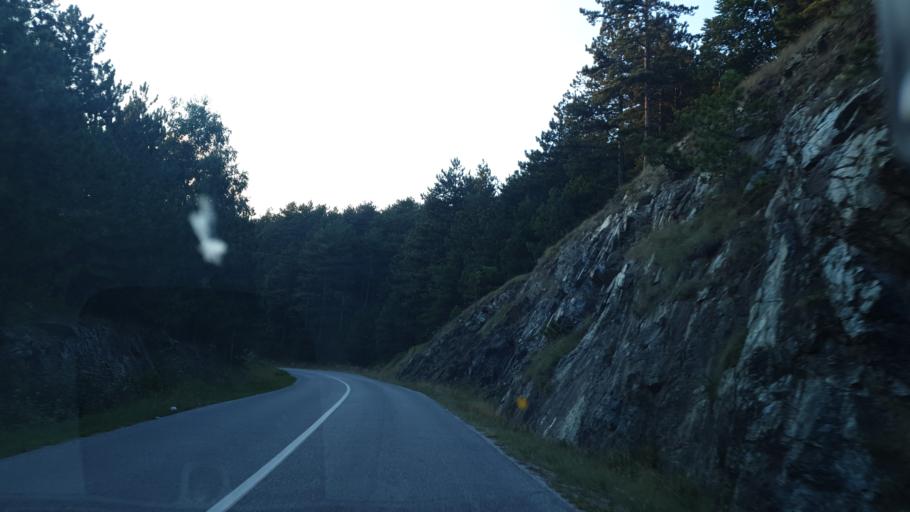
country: RS
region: Central Serbia
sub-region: Zlatiborski Okrug
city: Kosjeric
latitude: 44.0910
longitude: 19.9928
